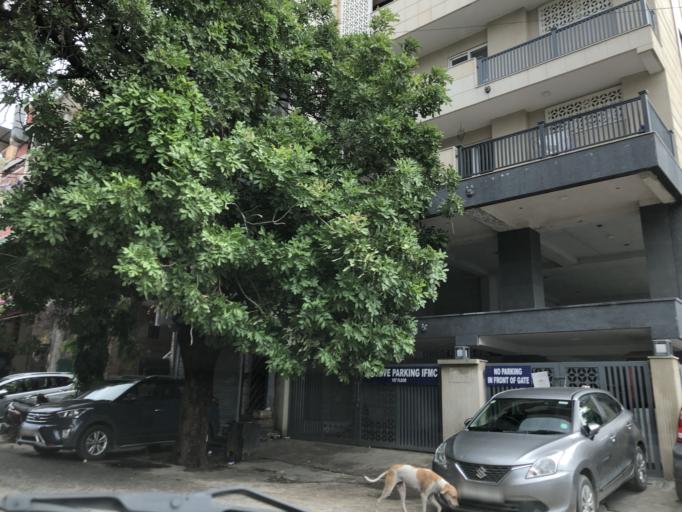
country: IN
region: NCT
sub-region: New Delhi
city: New Delhi
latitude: 28.5728
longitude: 77.2415
